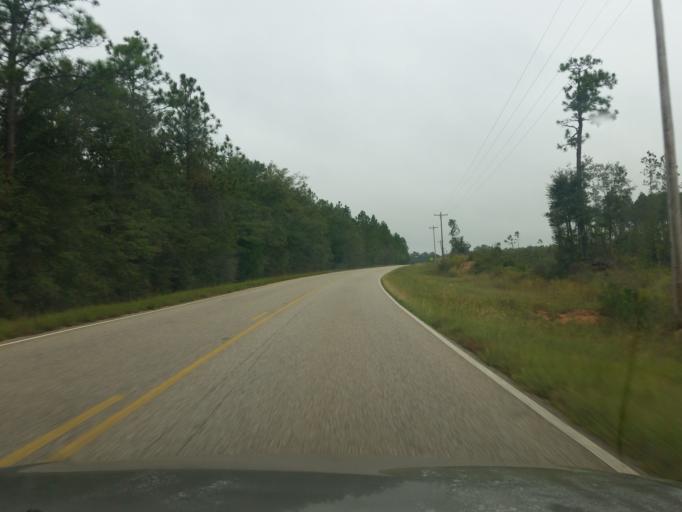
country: US
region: Florida
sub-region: Escambia County
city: Cantonment
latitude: 30.6285
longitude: -87.4351
